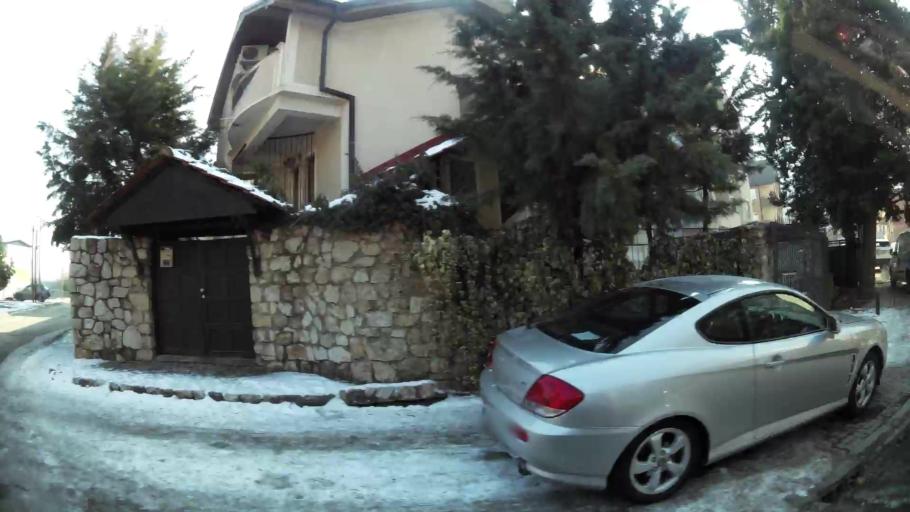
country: MK
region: Kisela Voda
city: Usje
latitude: 41.9722
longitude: 21.4423
